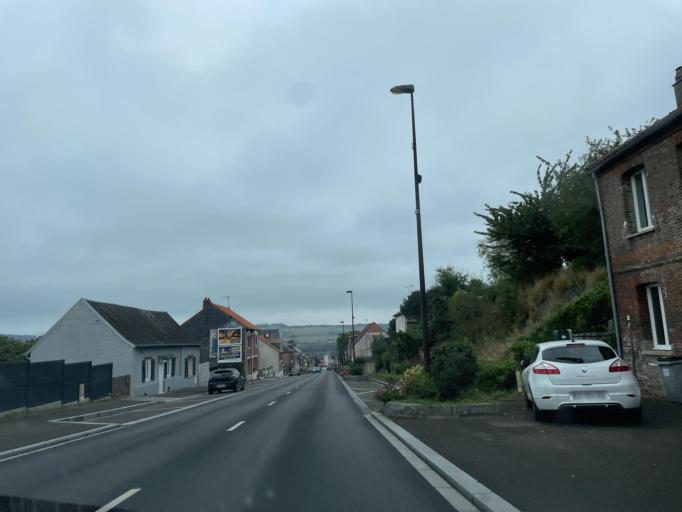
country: FR
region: Haute-Normandie
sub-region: Departement de la Seine-Maritime
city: Eu
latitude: 50.0399
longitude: 1.4149
